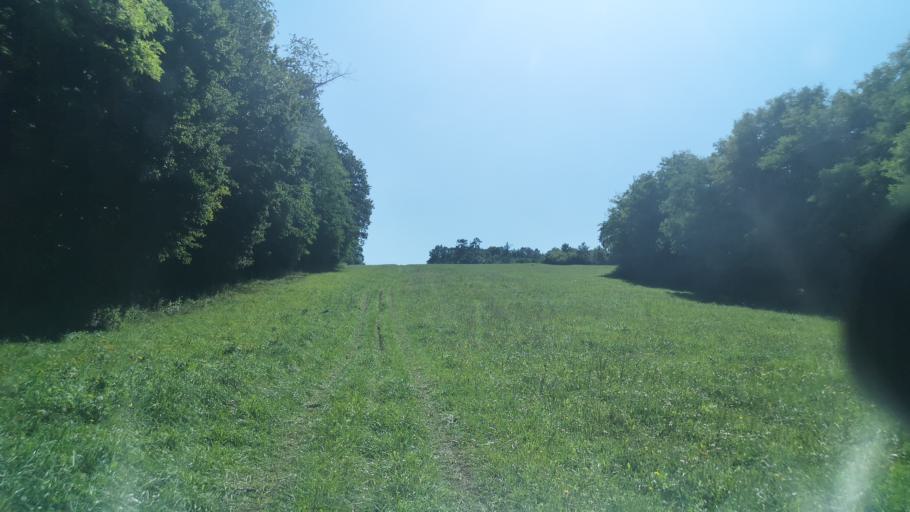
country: SK
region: Trnavsky
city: Smolenice
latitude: 48.5804
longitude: 17.4303
